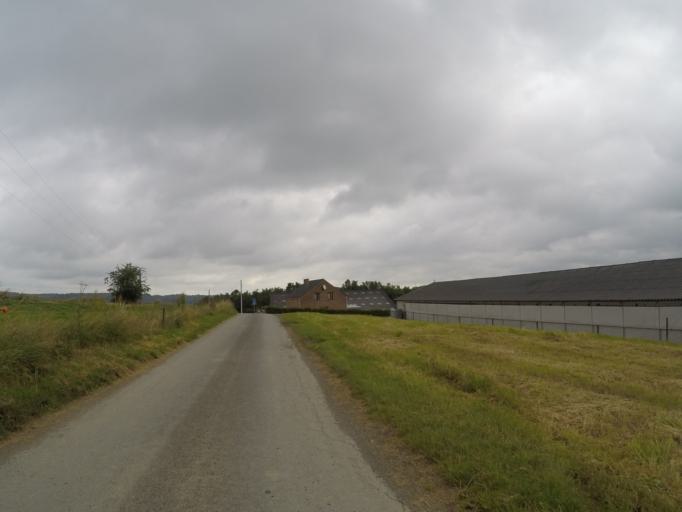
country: BE
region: Wallonia
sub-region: Province de Namur
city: Yvoir
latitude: 50.3292
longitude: 4.9130
